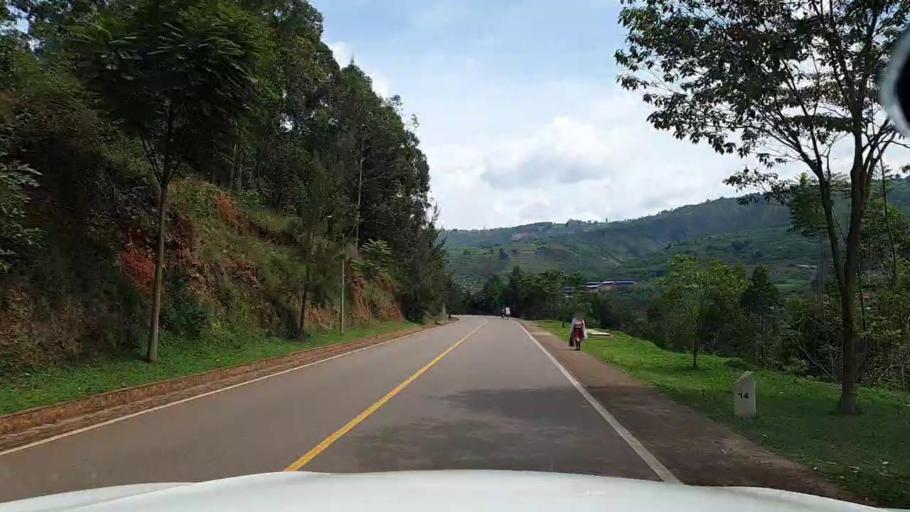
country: RW
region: Kigali
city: Kigali
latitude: -1.8590
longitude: 30.0940
